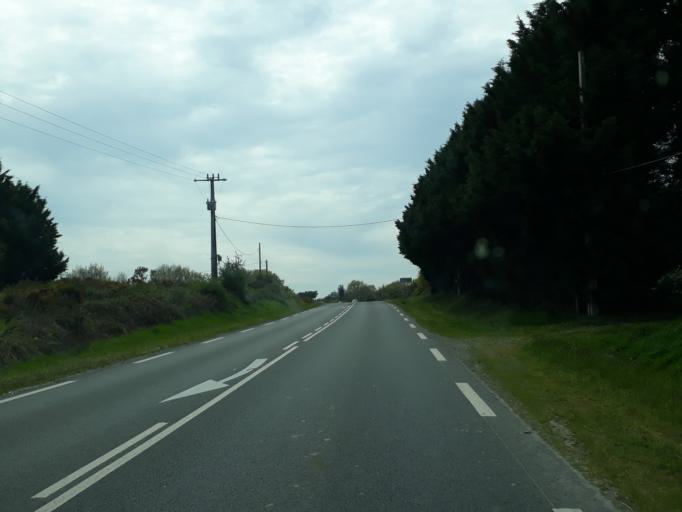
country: FR
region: Pays de la Loire
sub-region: Departement de la Loire-Atlantique
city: Guerande
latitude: 47.3470
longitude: -2.4264
